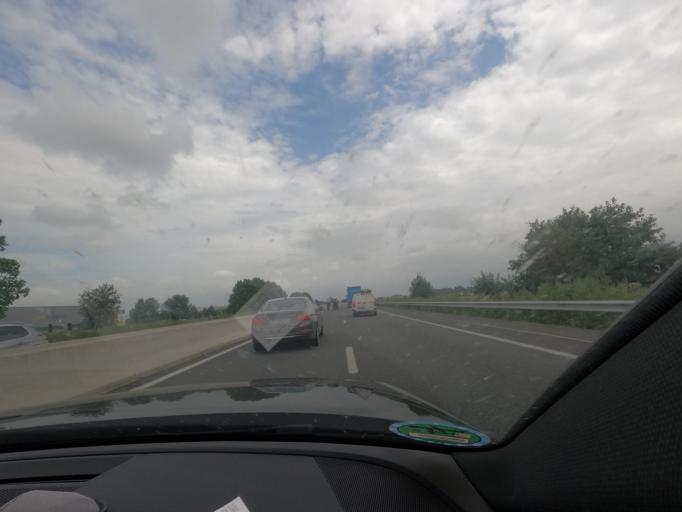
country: FR
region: Nord-Pas-de-Calais
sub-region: Departement du Nord
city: Neuville-Saint-Remy
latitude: 50.1924
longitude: 3.2023
